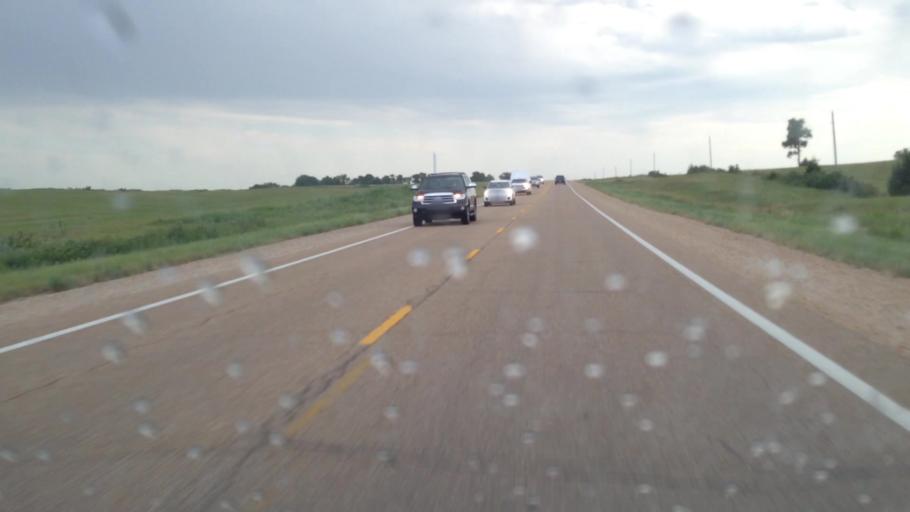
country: US
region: Kansas
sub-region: Coffey County
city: Burlington
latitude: 38.1475
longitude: -95.7392
